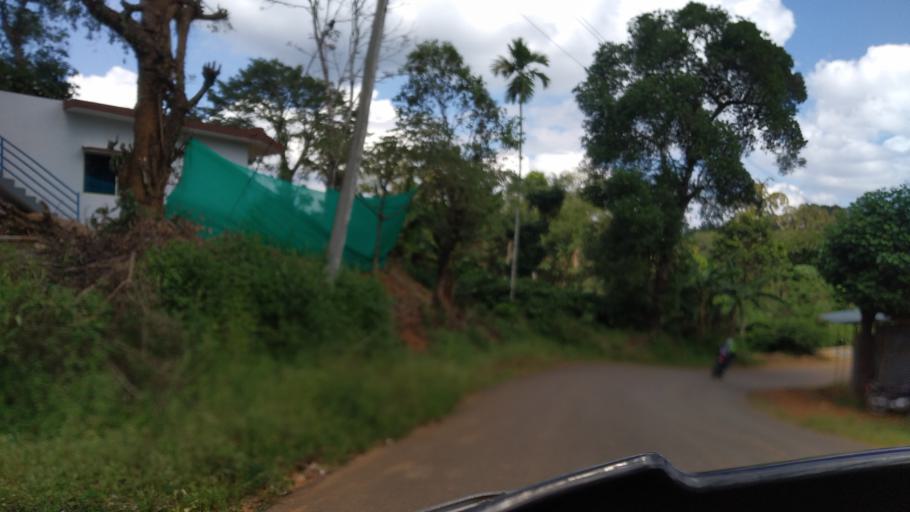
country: IN
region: Karnataka
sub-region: Kodagu
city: Ponnampet
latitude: 12.0360
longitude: 75.9151
